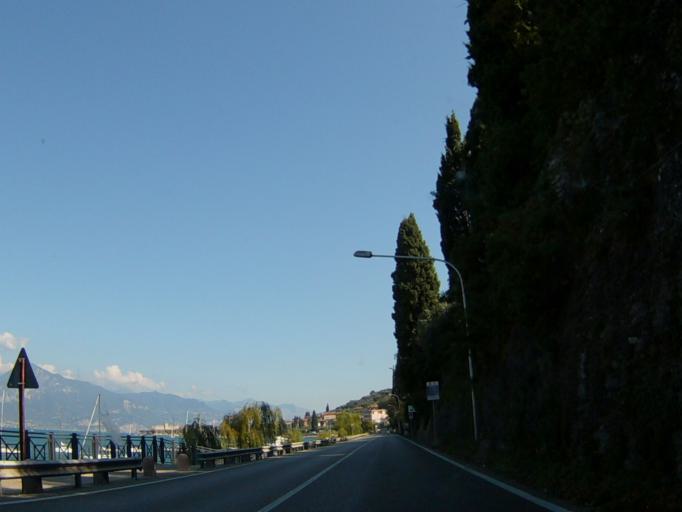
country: IT
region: Veneto
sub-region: Provincia di Verona
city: Torri del Benaco
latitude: 45.5964
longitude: 10.6830
